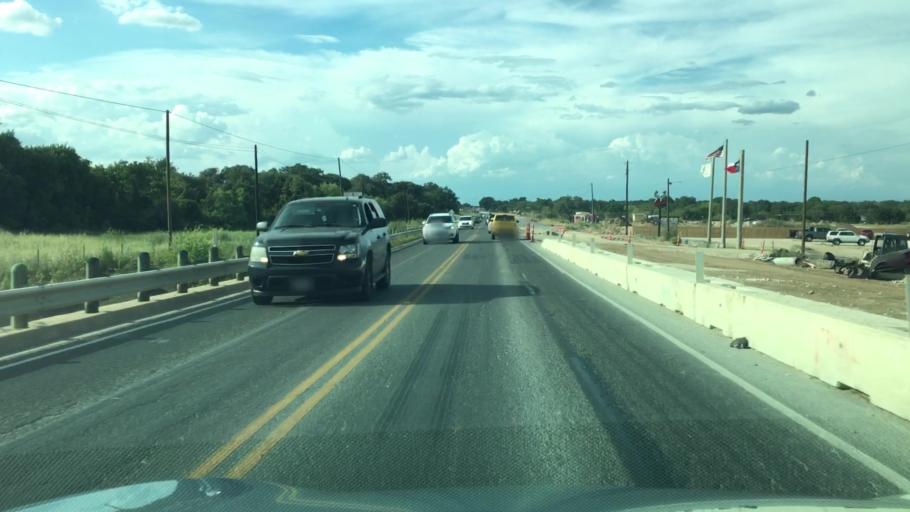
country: US
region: Texas
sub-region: Hays County
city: Buda
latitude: 30.0699
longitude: -97.8742
